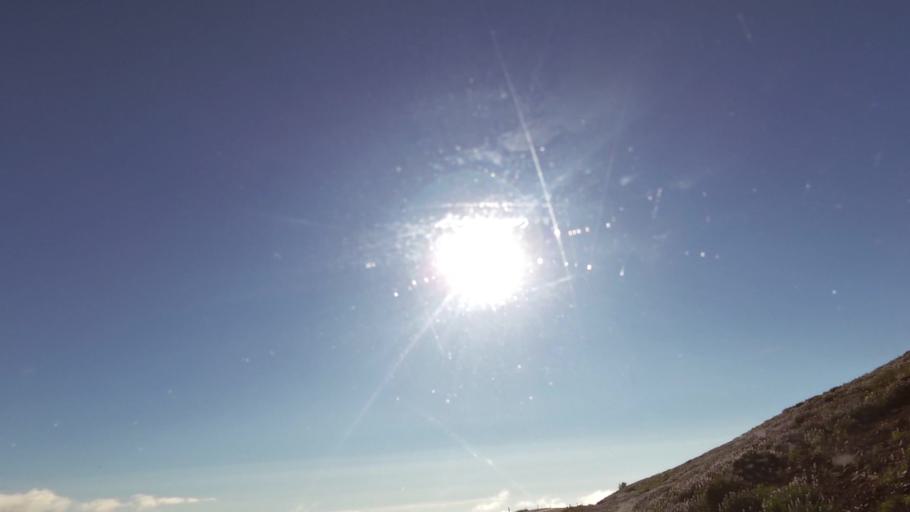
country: IS
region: West
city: Olafsvik
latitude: 65.5382
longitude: -23.8044
